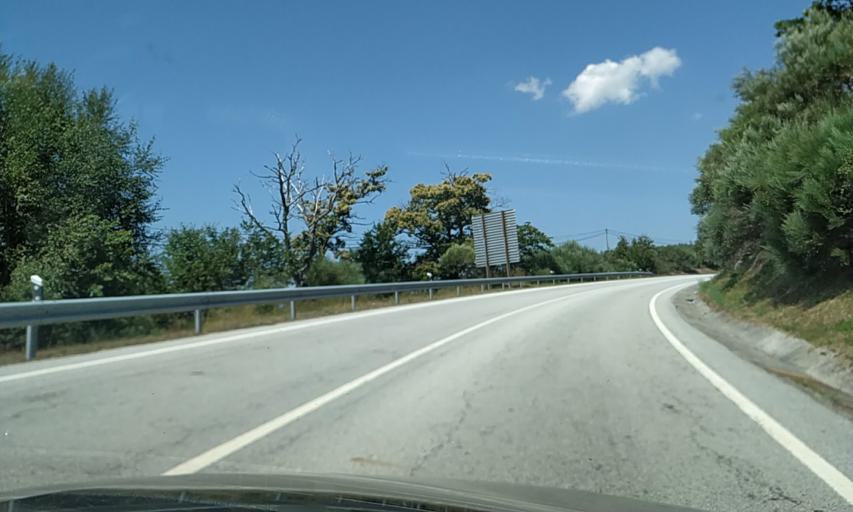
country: PT
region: Viseu
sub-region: Castro Daire
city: Castro Daire
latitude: 40.9413
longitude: -7.9114
